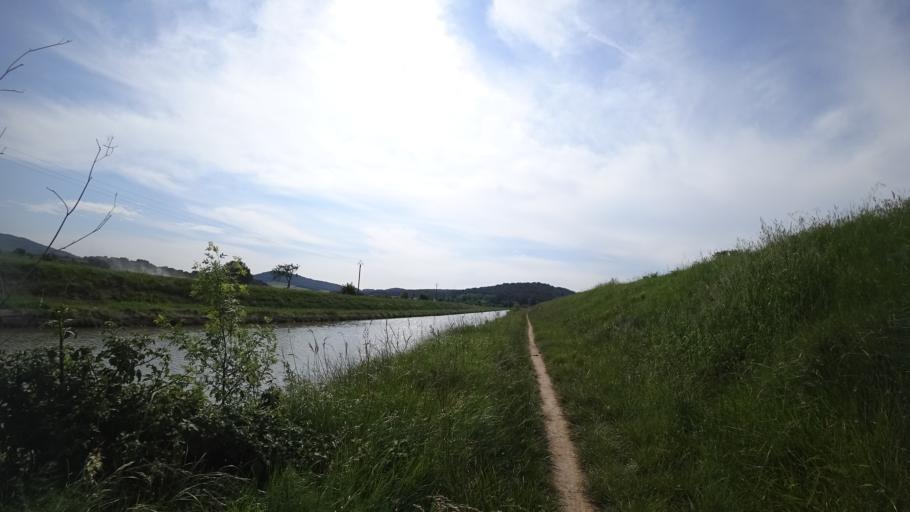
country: FR
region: Languedoc-Roussillon
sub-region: Departement de l'Herault
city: Olonzac
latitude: 43.2653
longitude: 2.7427
